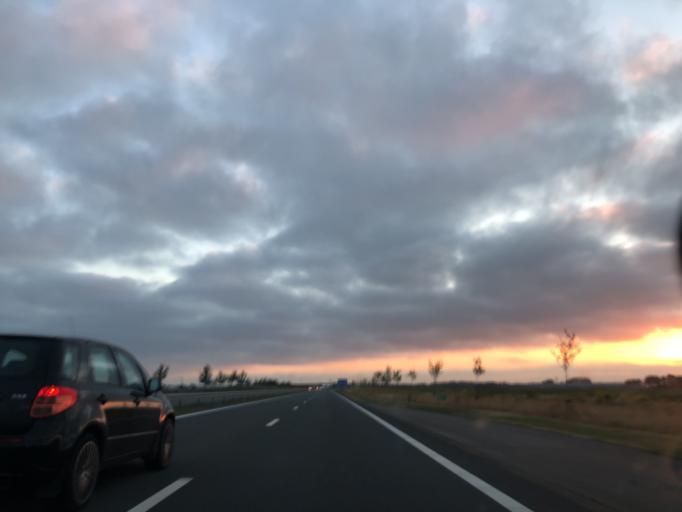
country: NL
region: Groningen
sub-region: Gemeente Veendam
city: Veendam
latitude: 53.0707
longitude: 6.8780
